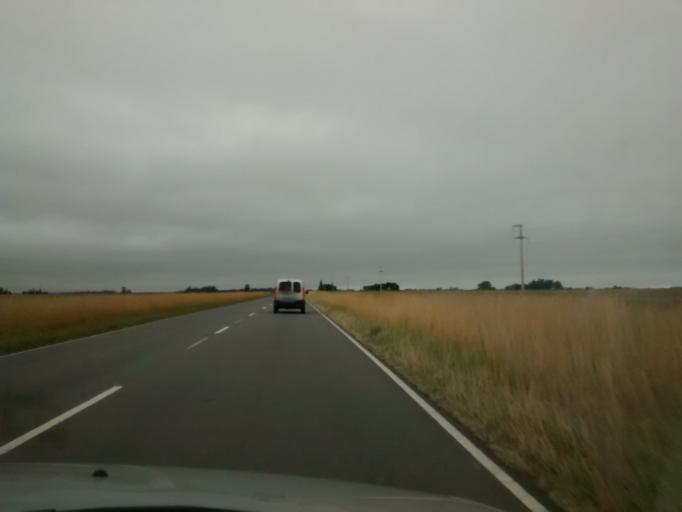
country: AR
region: Buenos Aires
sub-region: Partido de Ayacucho
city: Ayacucho
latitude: -37.0221
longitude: -58.5387
